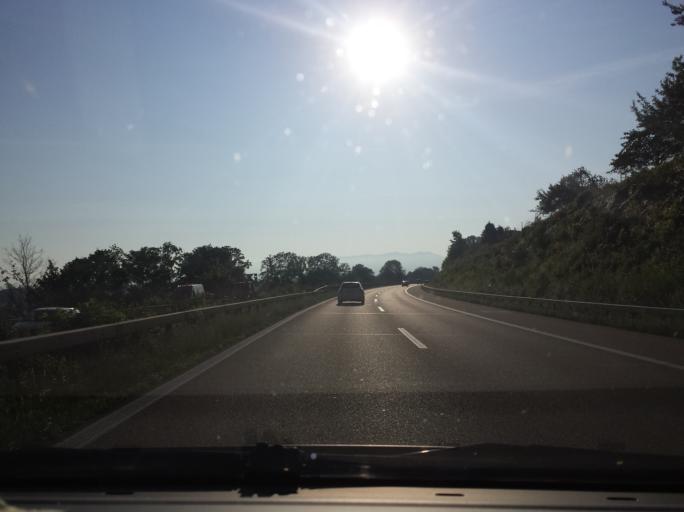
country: CH
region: Saint Gallen
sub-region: Wahlkreis Rheintal
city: Rheineck
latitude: 47.4767
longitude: 9.5570
